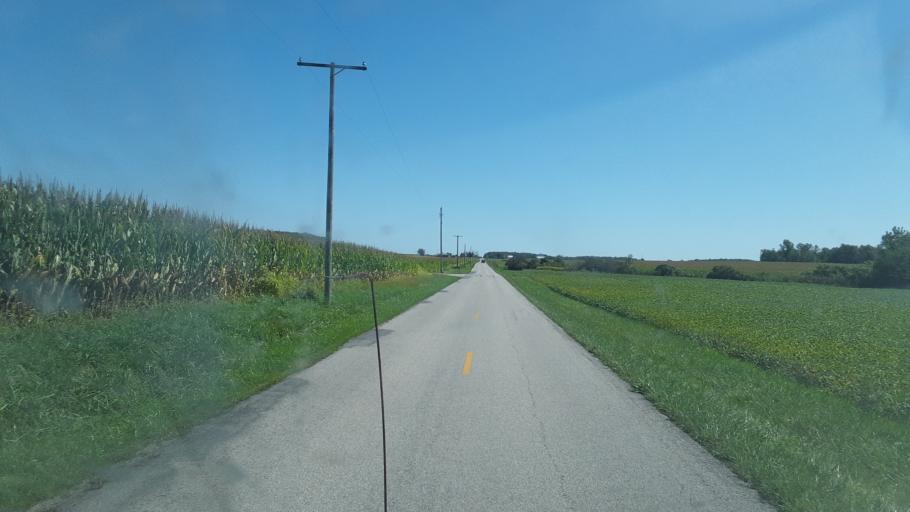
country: US
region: Ohio
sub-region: Sandusky County
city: Mount Carmel
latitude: 41.1610
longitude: -82.9173
